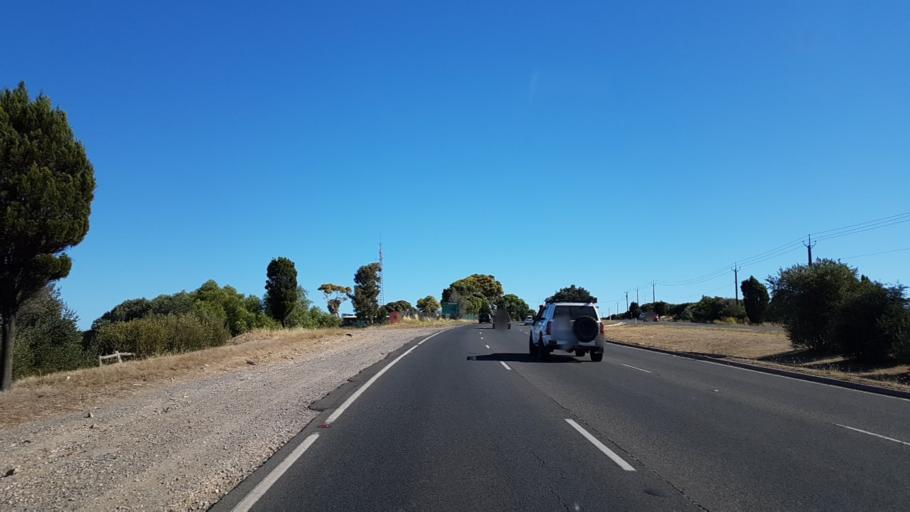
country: AU
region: South Australia
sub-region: Onkaparinga
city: Bedford Park
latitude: -35.0452
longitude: 138.5610
